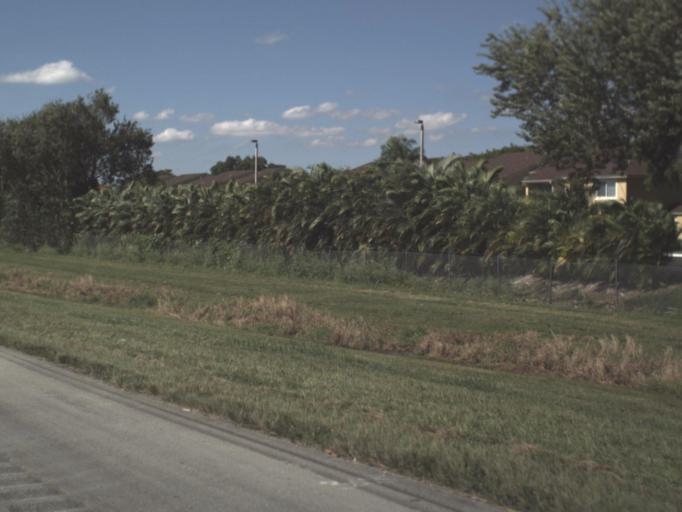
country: US
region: Florida
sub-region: Miami-Dade County
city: Homestead
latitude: 25.4677
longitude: -80.4550
